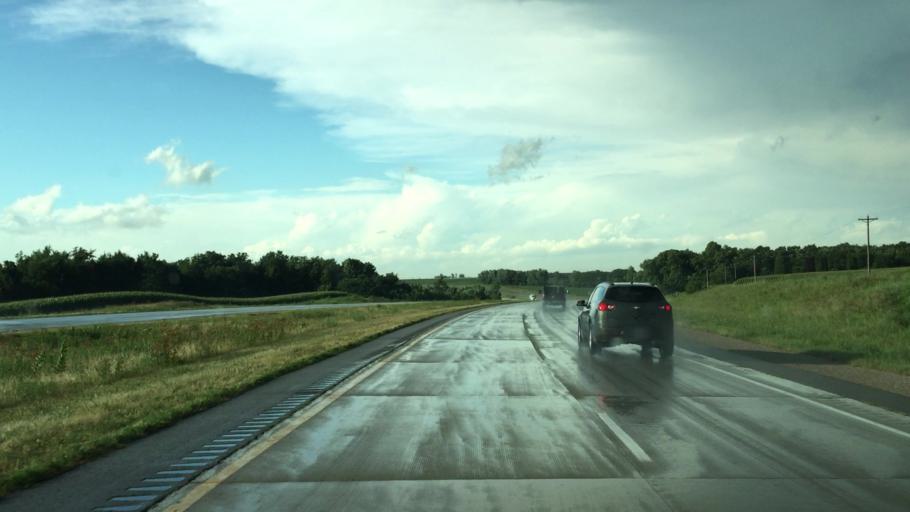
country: US
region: Iowa
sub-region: Henry County
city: Mount Pleasant
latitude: 41.0364
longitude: -91.5478
